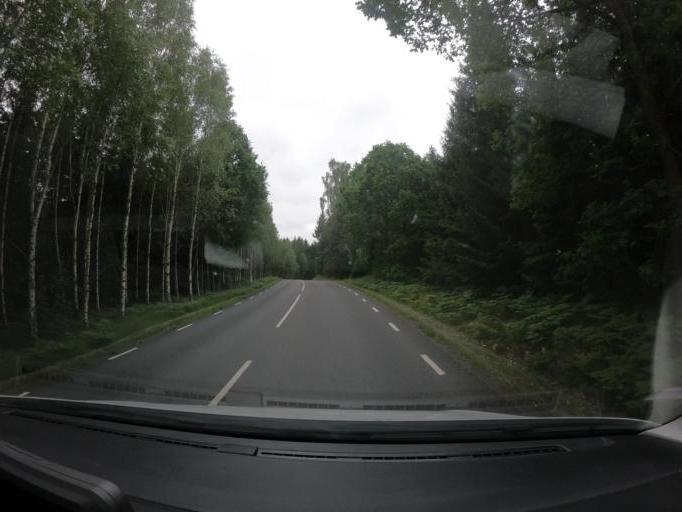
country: SE
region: Skane
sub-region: Perstorps Kommun
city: Perstorp
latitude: 56.1565
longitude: 13.3481
